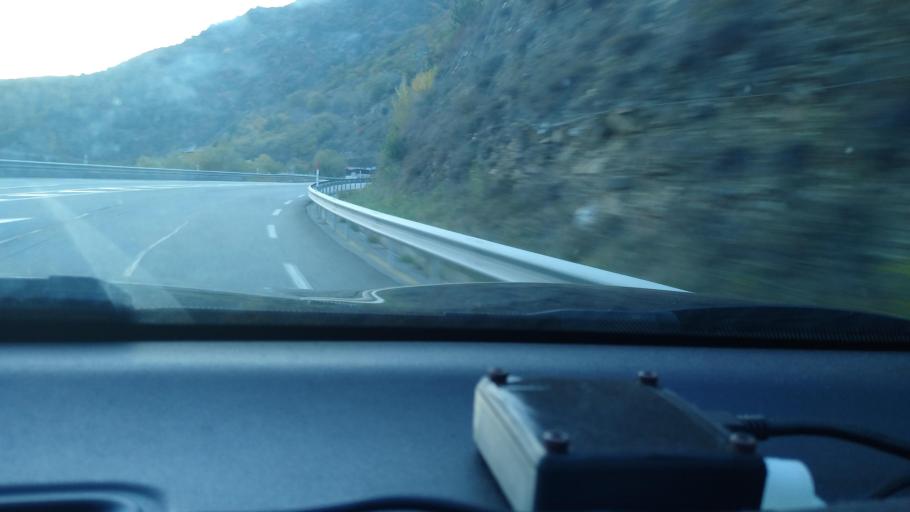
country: FR
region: Languedoc-Roussillon
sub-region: Departement des Pyrenees-Orientales
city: Vernet-les-Bains
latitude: 42.5131
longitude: 2.1886
